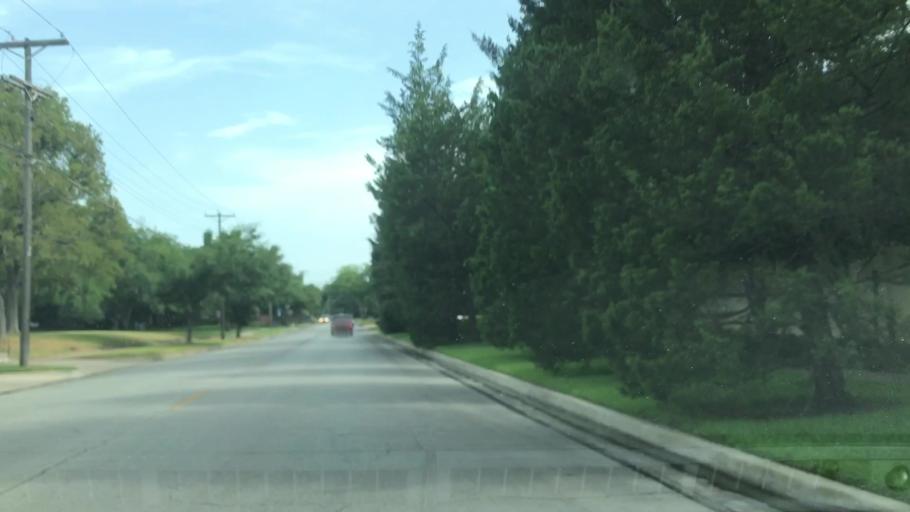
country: US
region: Texas
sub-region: Dallas County
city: Highland Park
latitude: 32.8261
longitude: -96.8070
